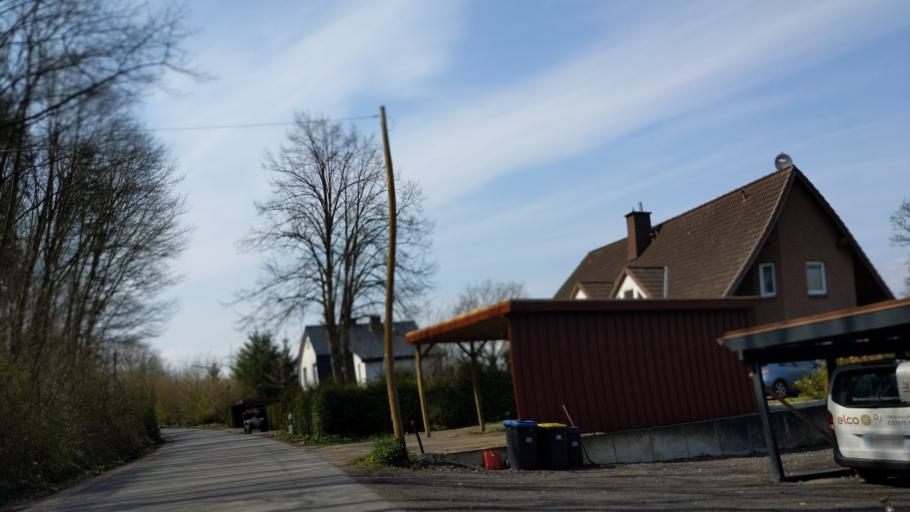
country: DE
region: Schleswig-Holstein
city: Ratekau
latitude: 53.9313
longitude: 10.7971
